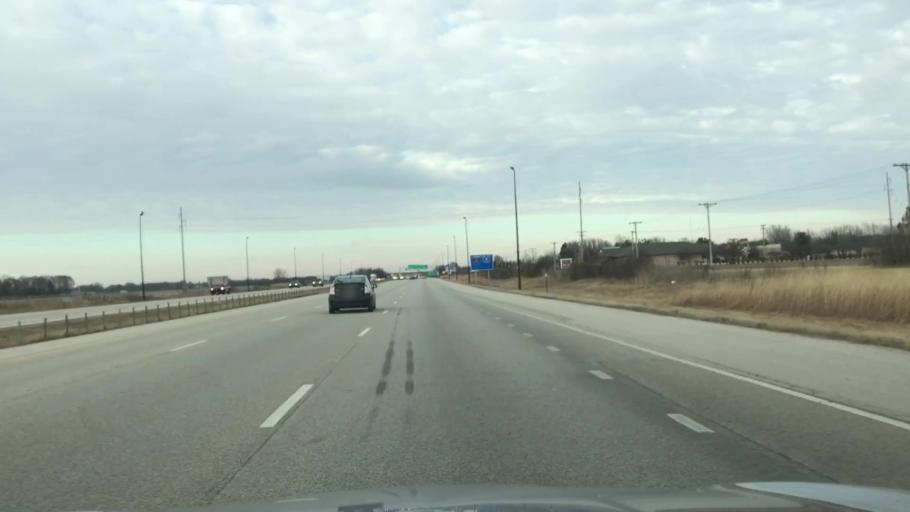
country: US
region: Illinois
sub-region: Sangamon County
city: Southern View
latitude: 39.7169
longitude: -89.6527
